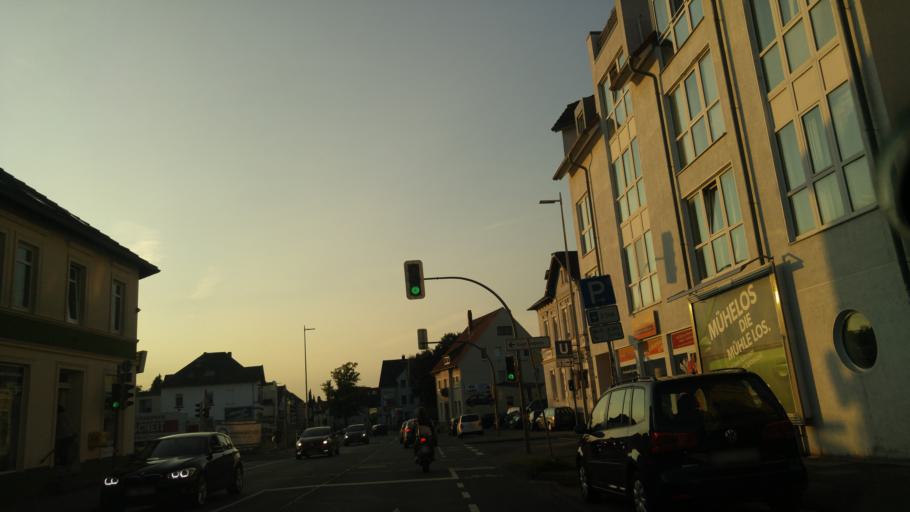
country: DE
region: North Rhine-Westphalia
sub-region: Regierungsbezirk Detmold
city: Bielefeld
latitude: 52.0319
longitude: 8.5270
